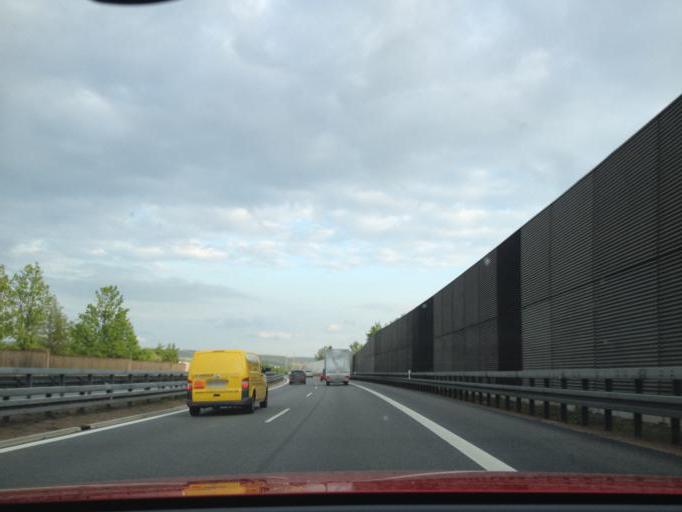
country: DE
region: Bavaria
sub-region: Upper Palatinate
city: Weiden
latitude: 49.6587
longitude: 12.1440
